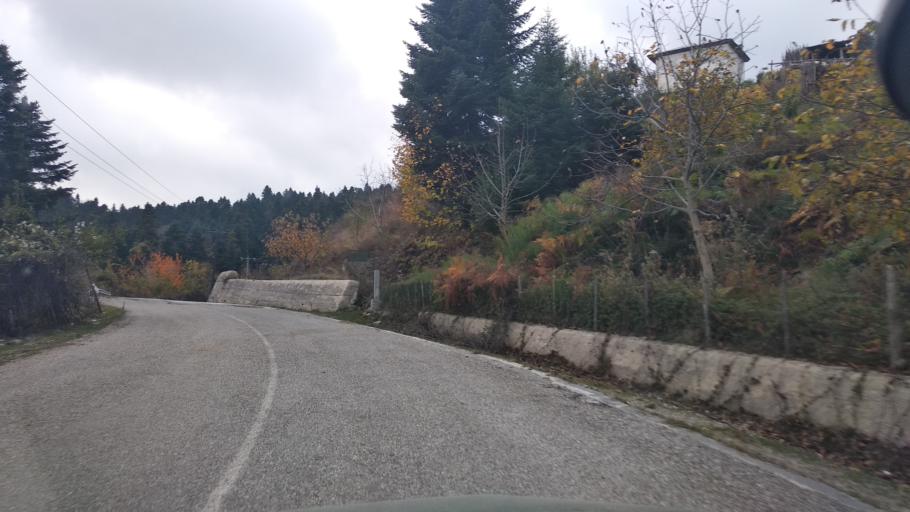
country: GR
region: Thessaly
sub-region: Trikala
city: Fiki
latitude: 39.5837
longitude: 21.4896
